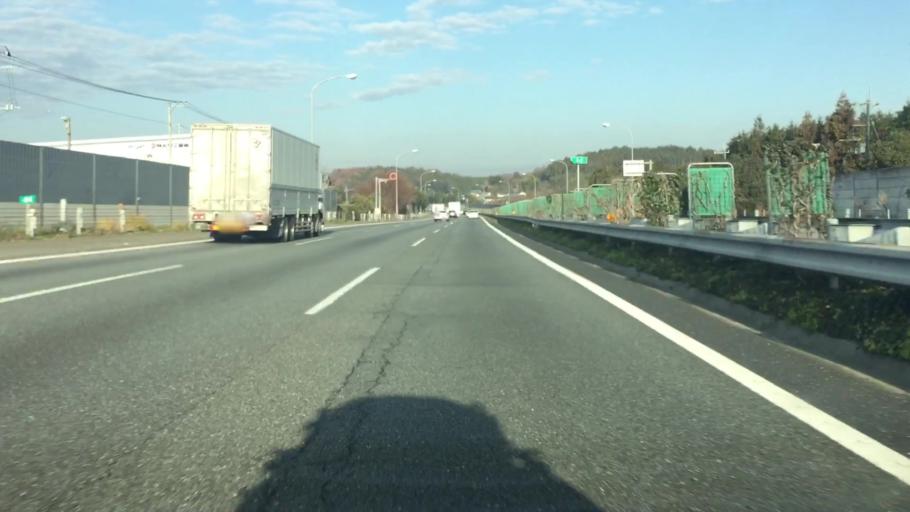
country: JP
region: Saitama
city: Ogawa
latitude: 36.0495
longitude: 139.3439
